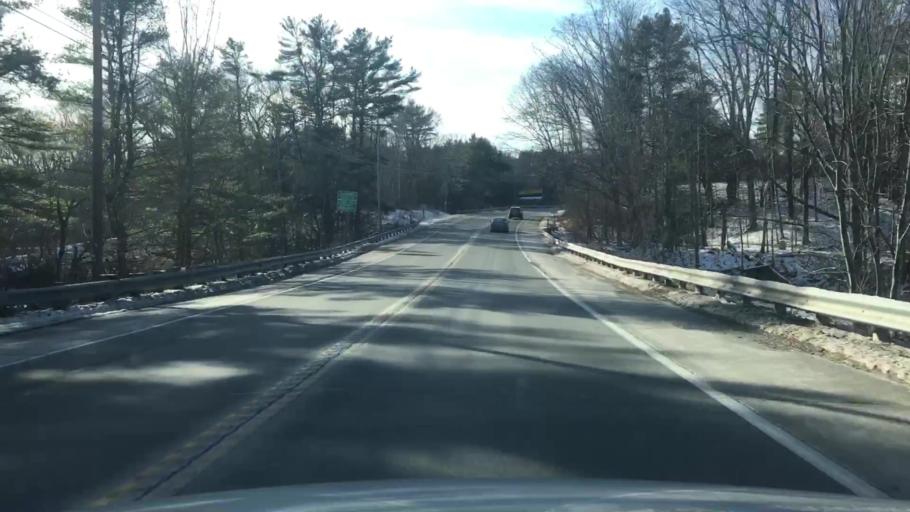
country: US
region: Maine
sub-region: Lincoln County
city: Wiscasset
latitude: 43.9653
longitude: -69.7207
